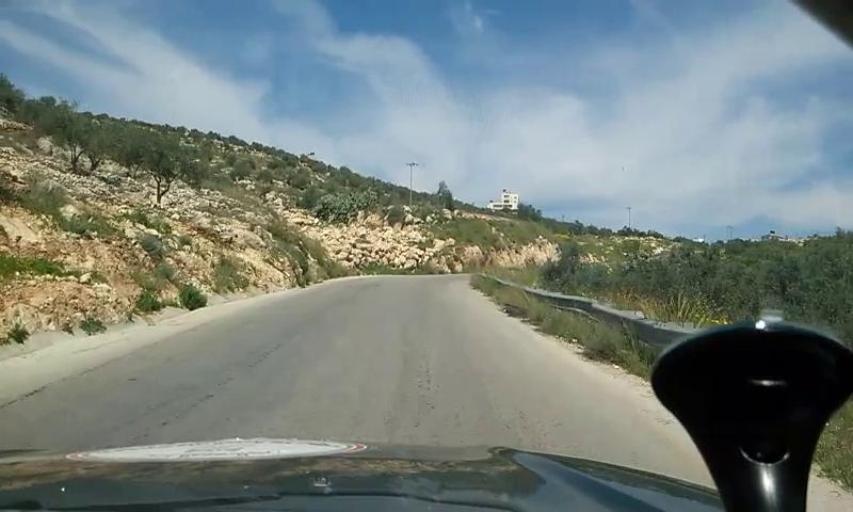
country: PS
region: West Bank
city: Kharbatha al Misbah
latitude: 31.8812
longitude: 35.0792
